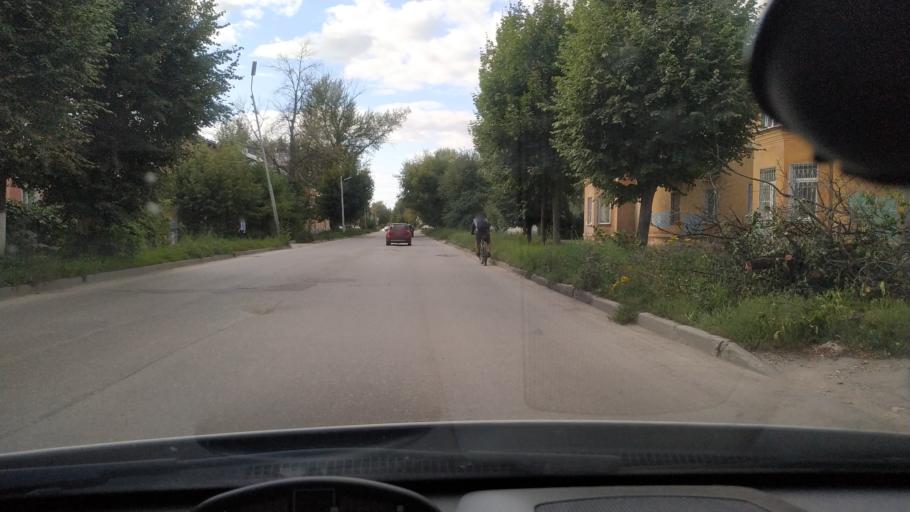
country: RU
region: Rjazan
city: Ryazan'
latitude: 54.6198
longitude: 39.7068
